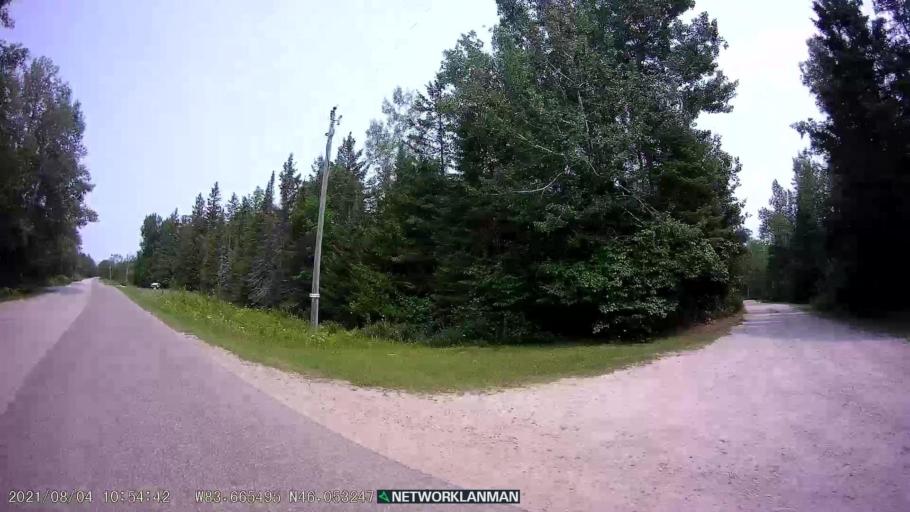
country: CA
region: Ontario
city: Thessalon
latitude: 46.0541
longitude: -83.6653
